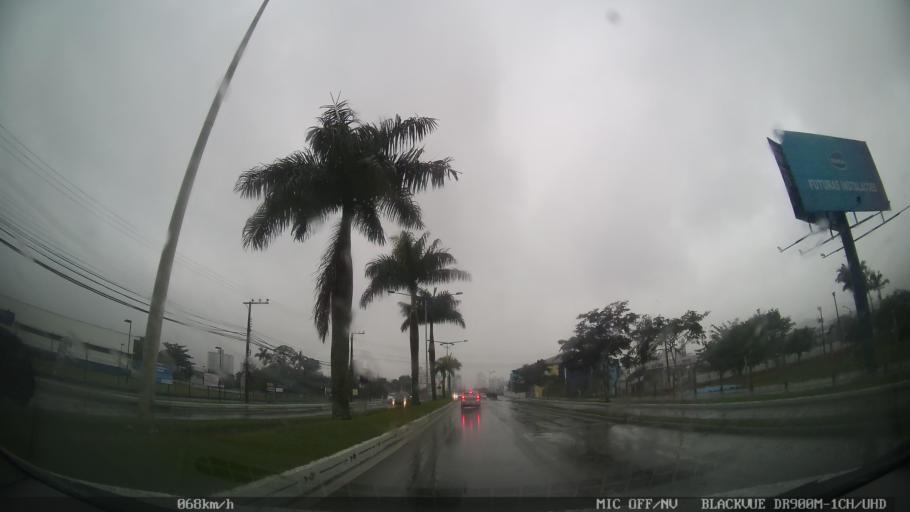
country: BR
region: Santa Catarina
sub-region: Itajai
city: Itajai
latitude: -26.9110
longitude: -48.6860
